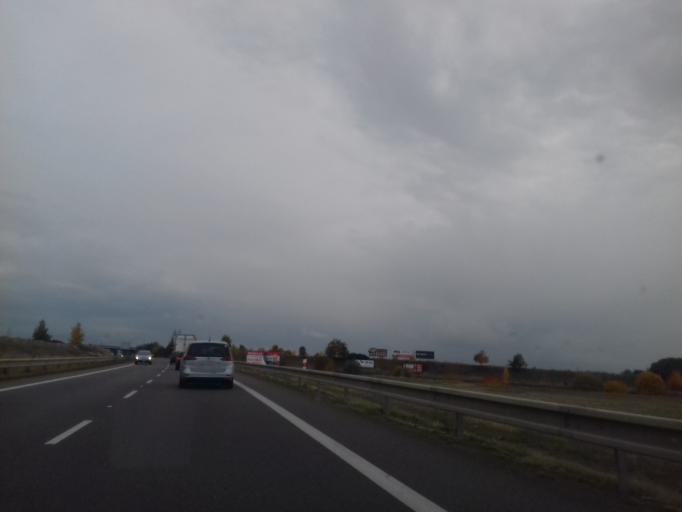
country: CZ
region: Pardubicky
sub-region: Okres Chrudim
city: Chrudim
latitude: 49.9896
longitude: 15.7694
